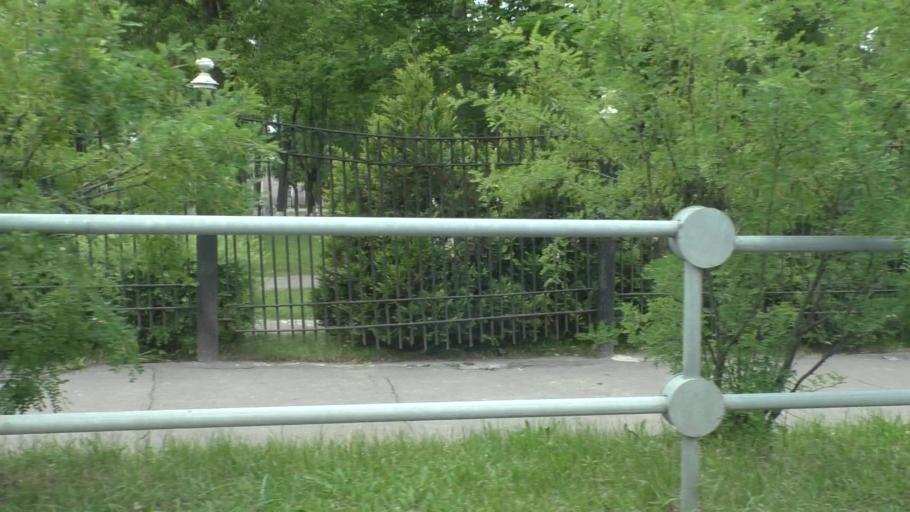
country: RU
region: Moskovskaya
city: Yegor'yevsk
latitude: 55.3869
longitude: 39.0299
